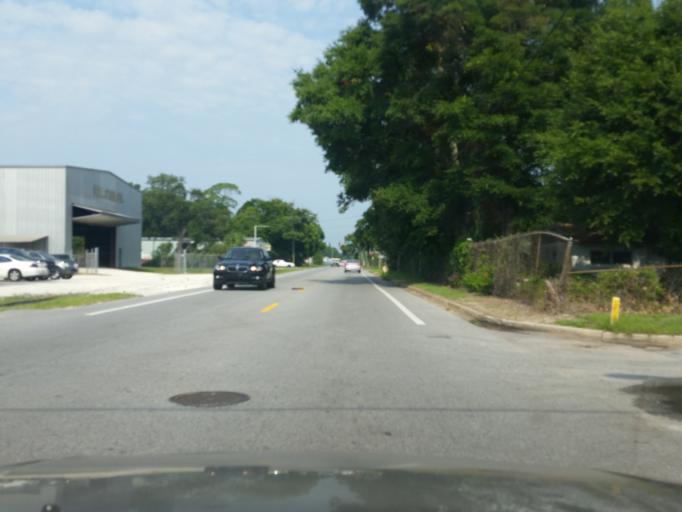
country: US
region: Florida
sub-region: Escambia County
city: Pensacola
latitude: 30.4055
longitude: -87.2286
